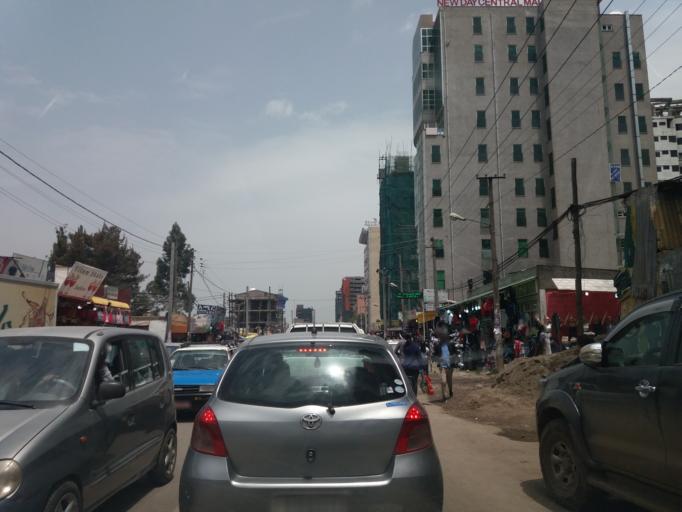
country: ET
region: Adis Abeba
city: Addis Ababa
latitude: 9.0120
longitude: 38.7878
